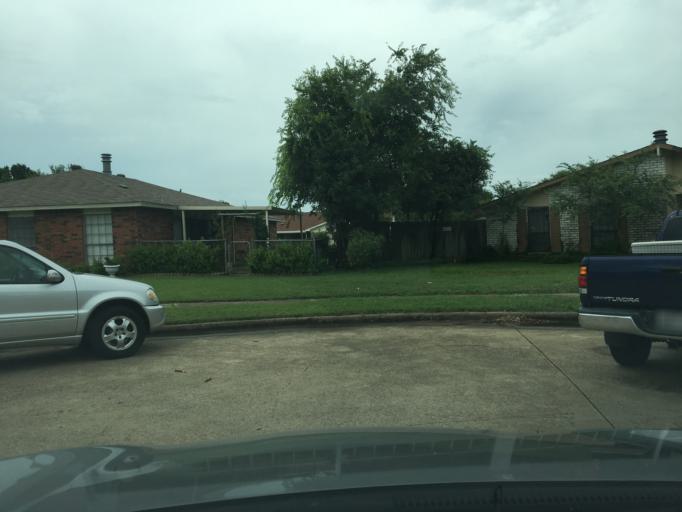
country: US
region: Texas
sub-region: Dallas County
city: Richardson
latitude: 32.9540
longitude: -96.6815
